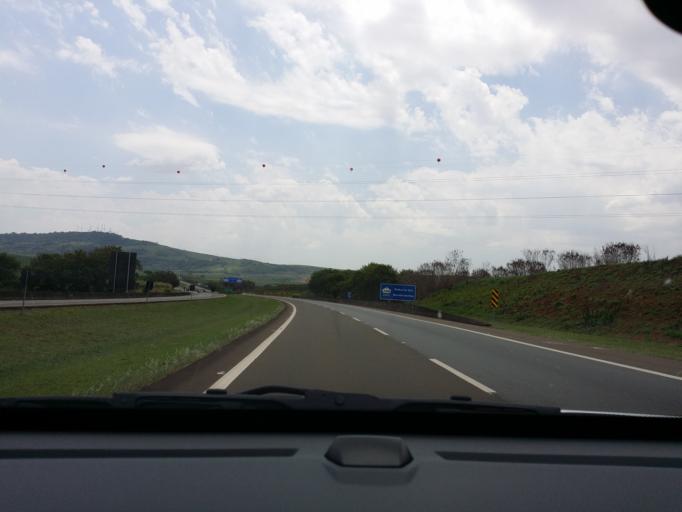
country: BR
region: Sao Paulo
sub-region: Limeira
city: Limeira
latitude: -22.5696
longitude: -47.4571
